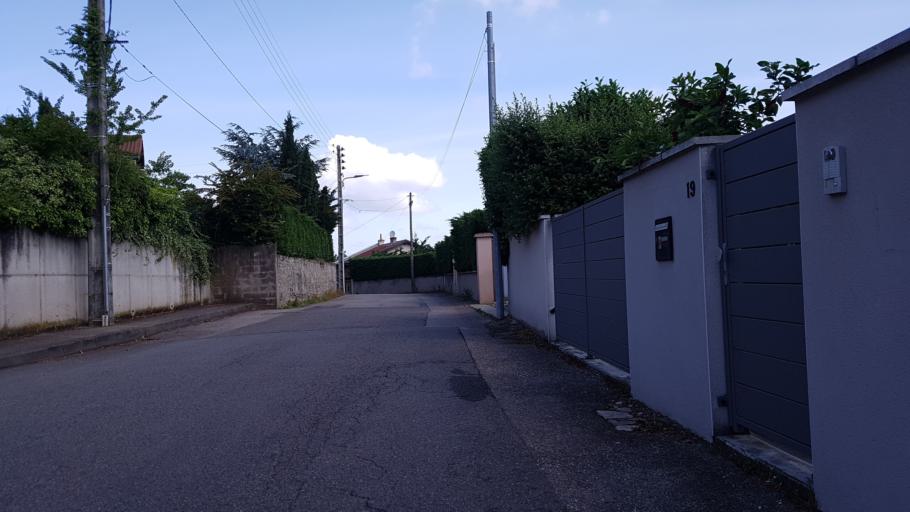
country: FR
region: Rhone-Alpes
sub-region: Departement du Rhone
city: Caluire-et-Cuire
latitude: 45.7939
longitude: 4.8548
